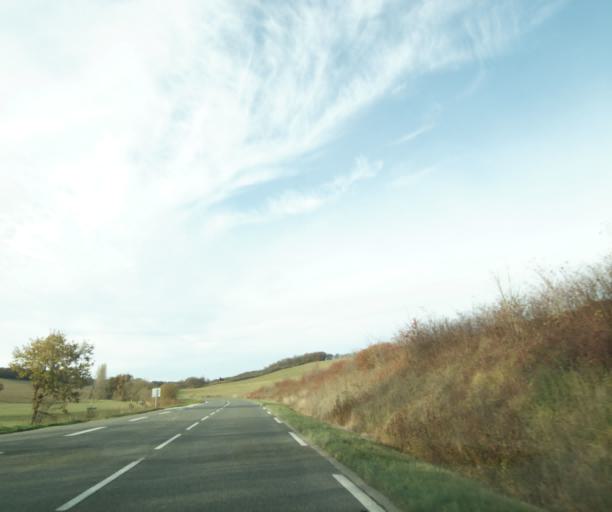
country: FR
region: Midi-Pyrenees
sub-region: Departement du Gers
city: Vic-Fezensac
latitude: 43.7363
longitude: 0.3601
